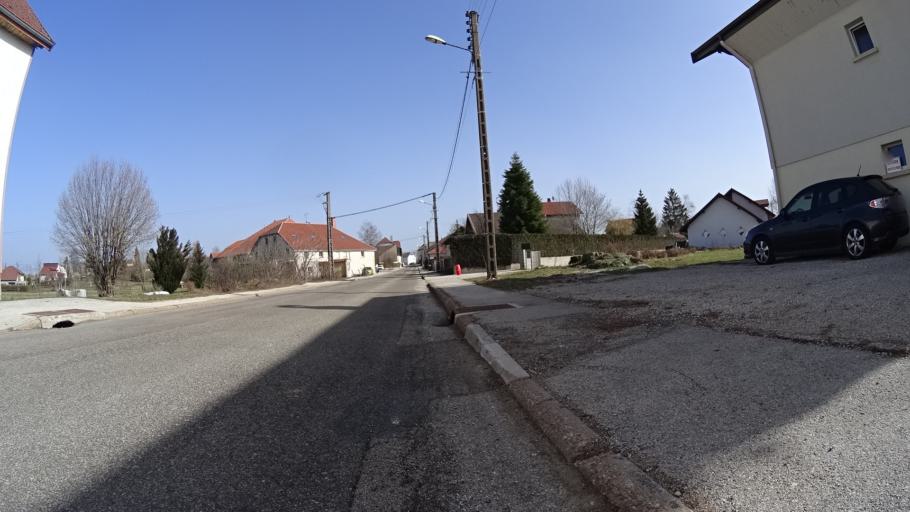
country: FR
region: Franche-Comte
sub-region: Departement du Doubs
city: Frasne
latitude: 46.8543
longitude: 6.1526
